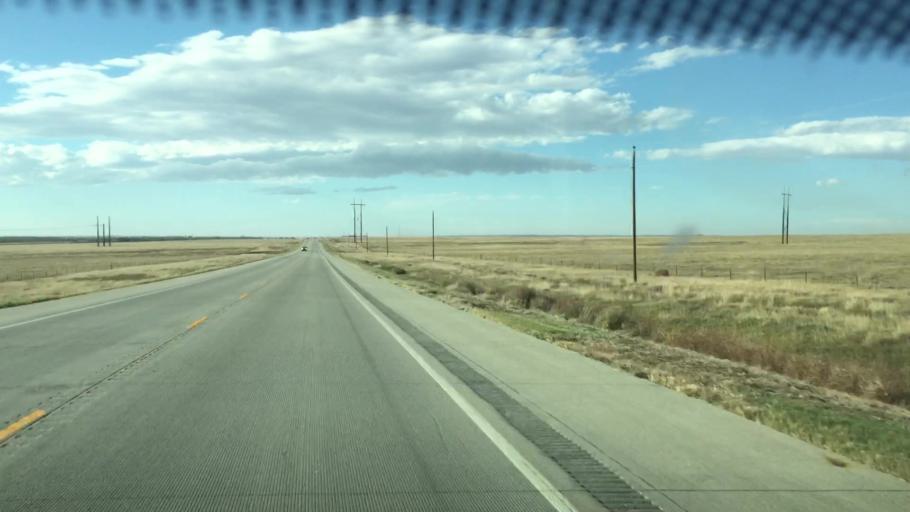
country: US
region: Colorado
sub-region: Lincoln County
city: Hugo
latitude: 39.0916
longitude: -103.4015
